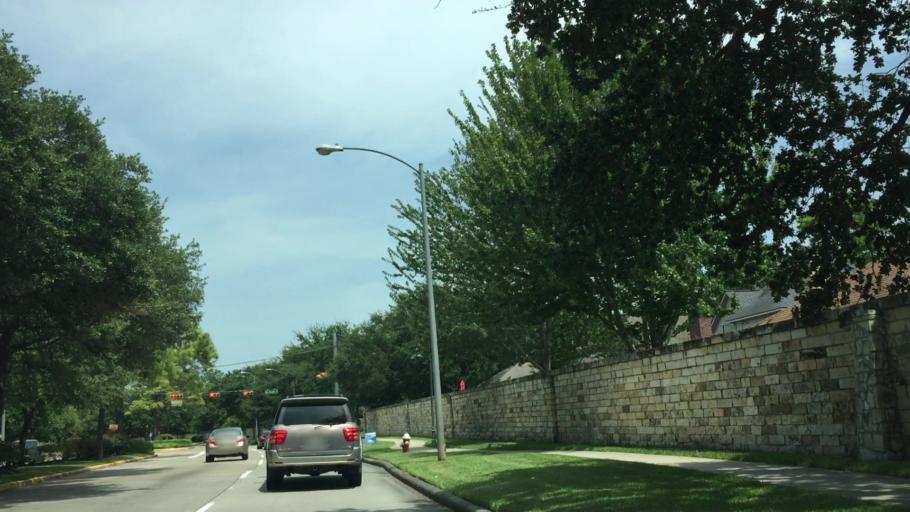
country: US
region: Texas
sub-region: Harris County
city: Jersey Village
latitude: 29.9088
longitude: -95.5745
